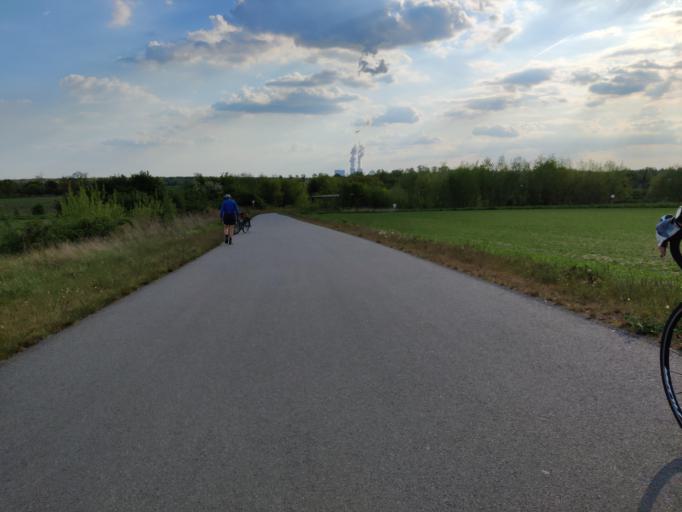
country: DE
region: Saxony
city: Espenhain
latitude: 51.2221
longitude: 12.4588
